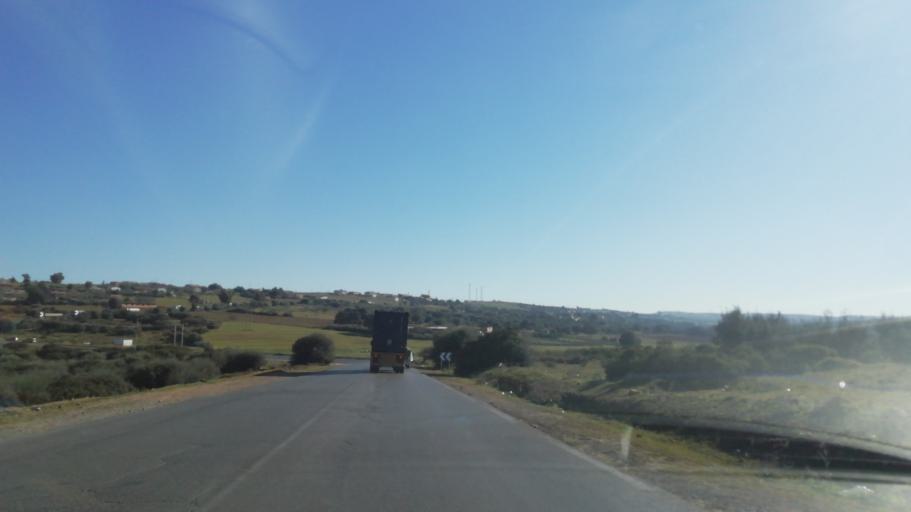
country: DZ
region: Relizane
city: Smala
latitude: 35.6863
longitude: 0.7963
